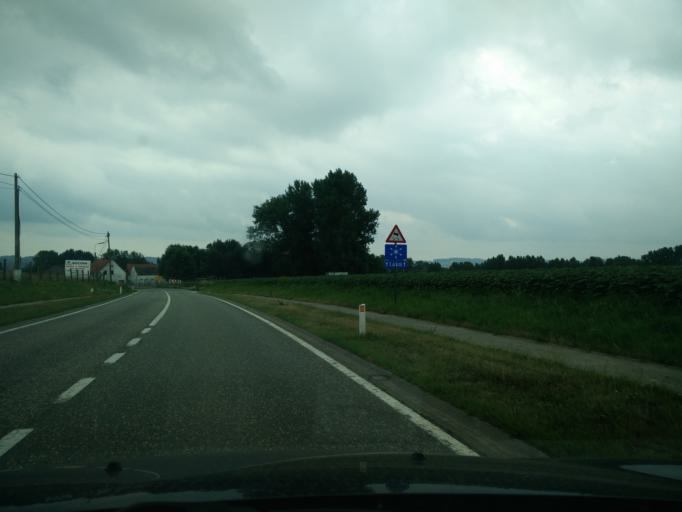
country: BE
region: Wallonia
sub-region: Province du Hainaut
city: Flobecq
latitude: 50.8104
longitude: 3.7366
